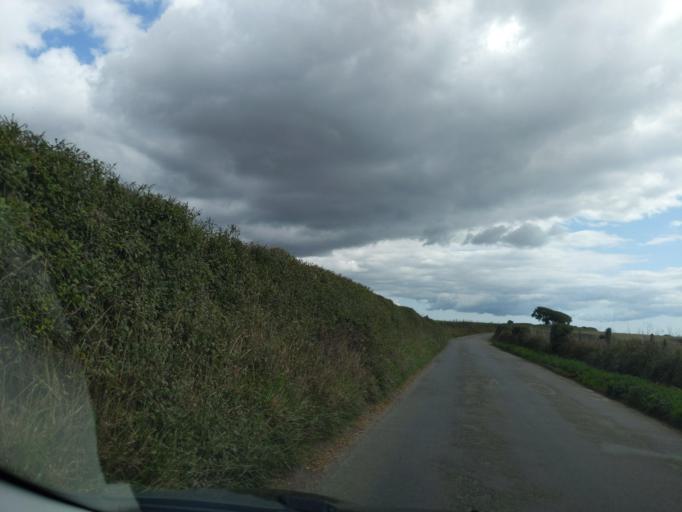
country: GB
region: England
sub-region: Plymouth
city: Plymstock
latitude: 50.3455
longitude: -4.1036
